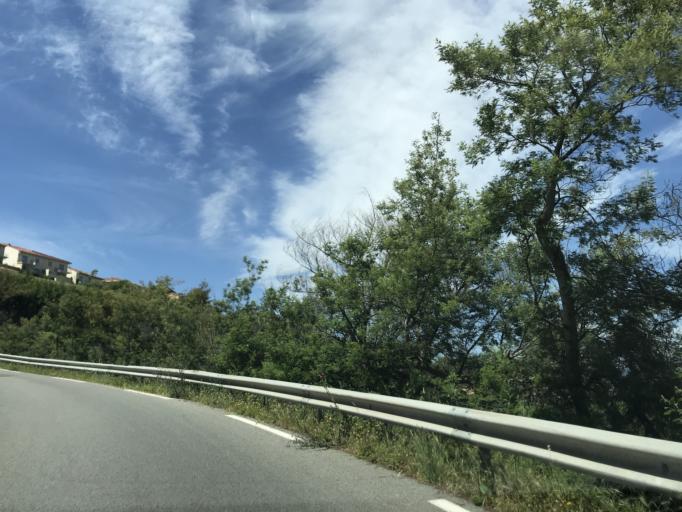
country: FR
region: Provence-Alpes-Cote d'Azur
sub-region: Departement du Var
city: Tanneron
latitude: 43.5891
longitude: 6.8795
